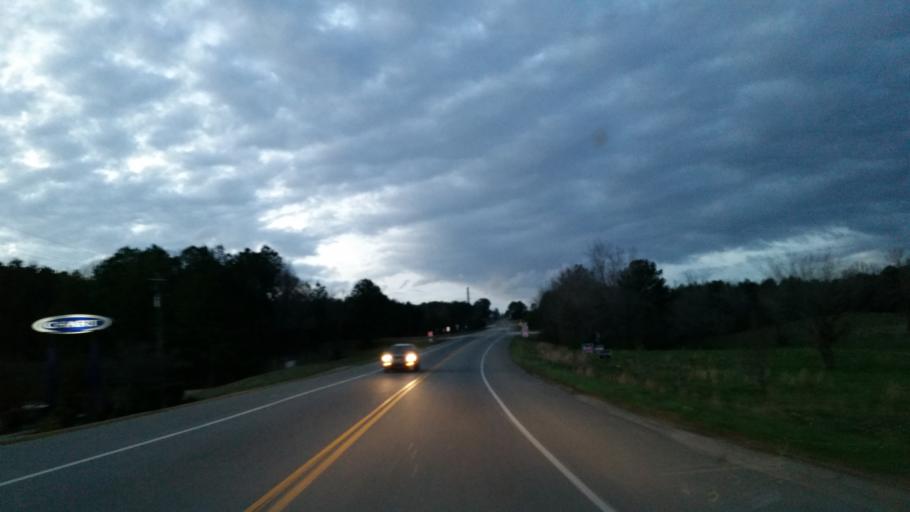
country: US
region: Georgia
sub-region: Cherokee County
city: Ball Ground
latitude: 34.2978
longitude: -84.4211
